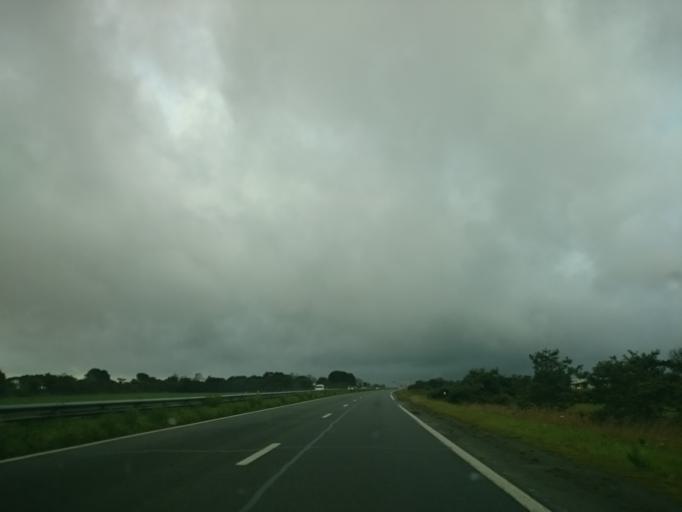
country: FR
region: Brittany
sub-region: Departement du Finistere
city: Gouesnou
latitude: 48.4345
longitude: -4.4364
